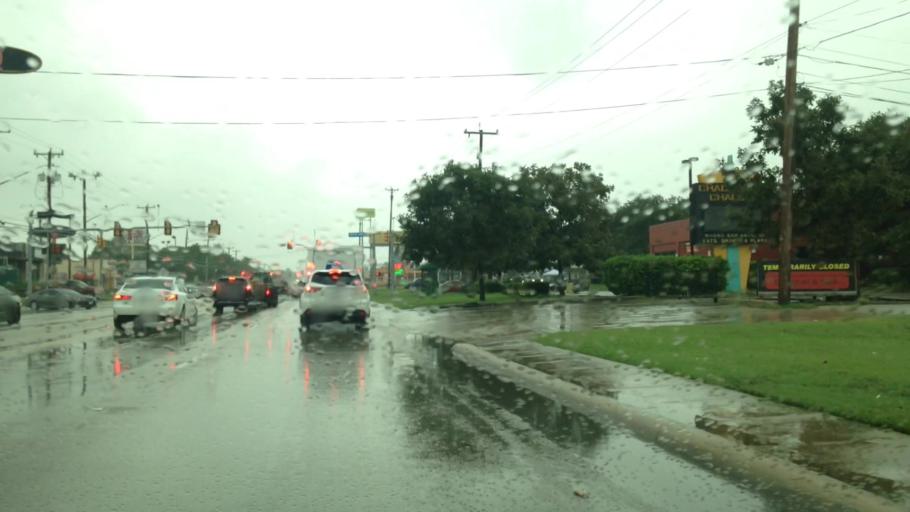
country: US
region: Texas
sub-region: Bexar County
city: Windcrest
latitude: 29.5175
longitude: -98.4109
